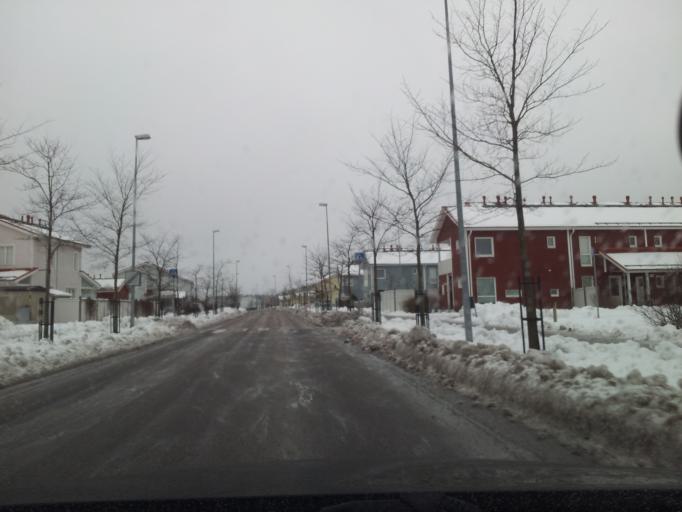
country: FI
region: Uusimaa
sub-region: Helsinki
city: Espoo
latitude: 60.1565
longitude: 24.5493
